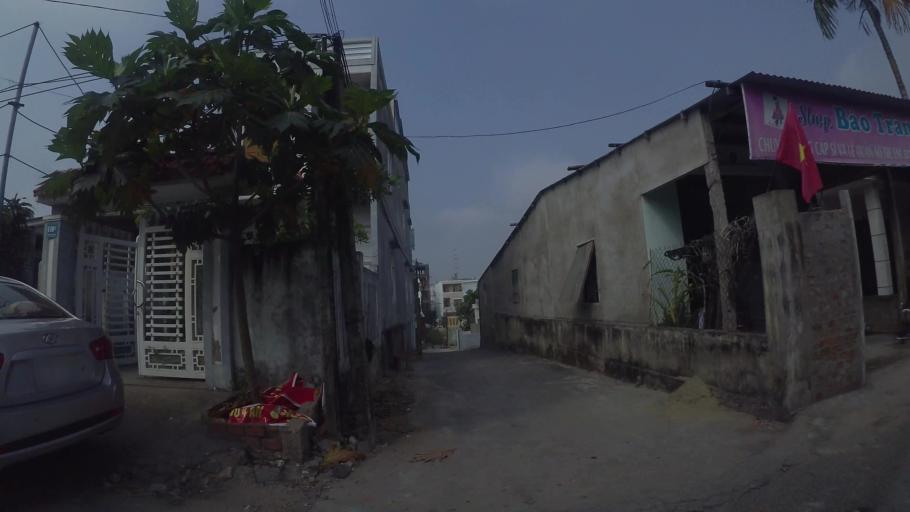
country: VN
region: Da Nang
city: Ngu Hanh Son
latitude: 16.0252
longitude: 108.2452
